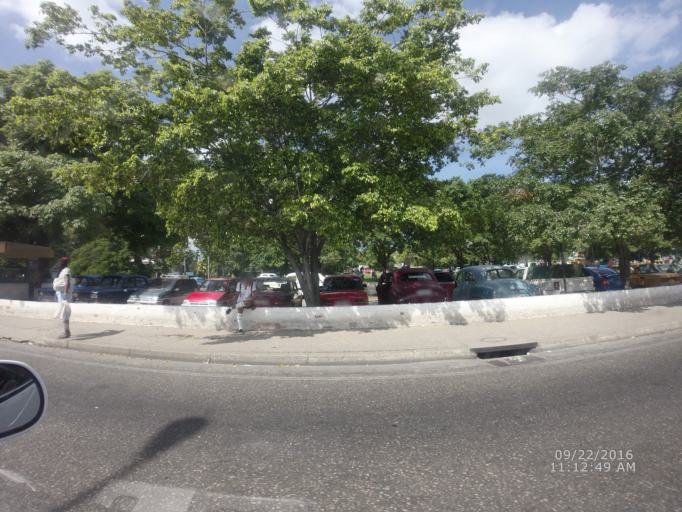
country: CU
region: La Habana
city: Cerro
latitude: 23.0929
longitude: -82.4216
